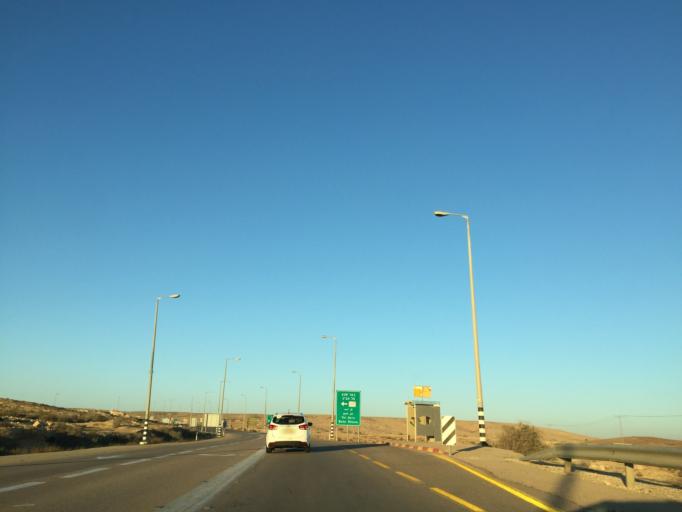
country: IL
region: Southern District
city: Midreshet Ben-Gurion
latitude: 30.8802
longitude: 34.7929
